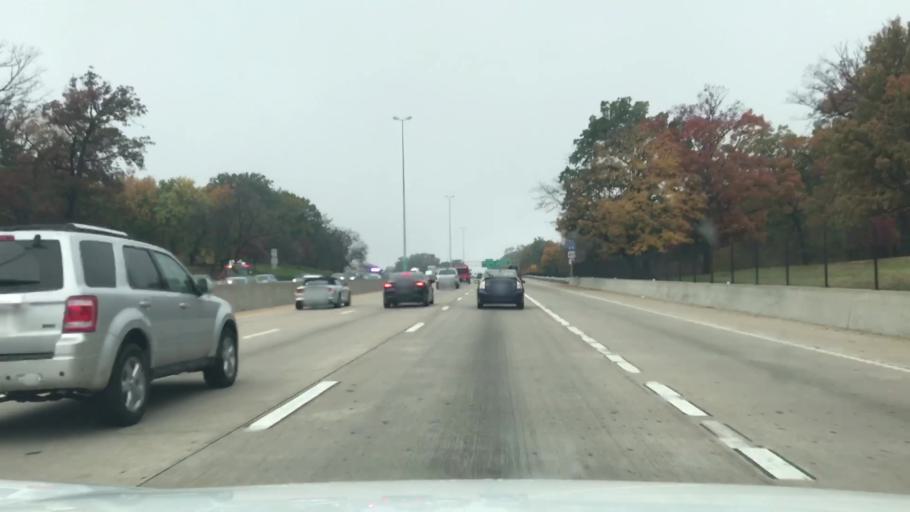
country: US
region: Missouri
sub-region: Saint Louis County
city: Richmond Heights
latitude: 38.6325
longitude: -90.2942
